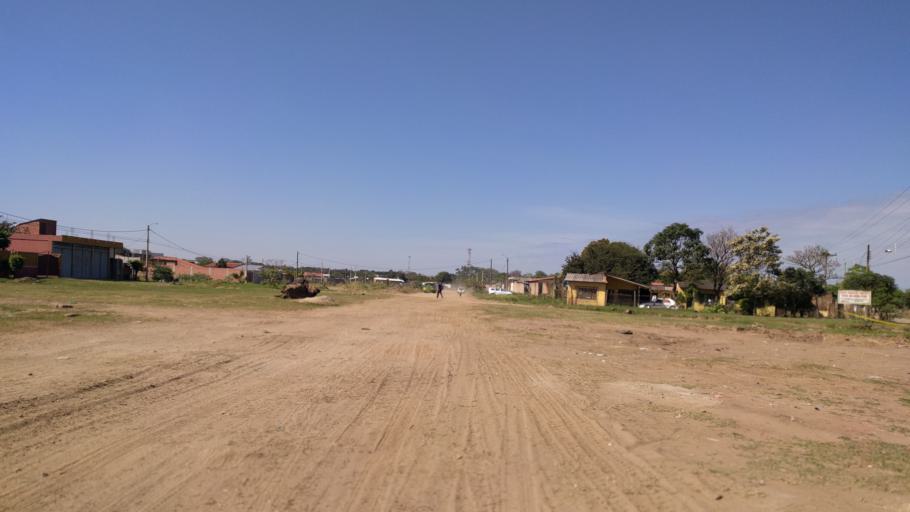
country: BO
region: Santa Cruz
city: Santa Cruz de la Sierra
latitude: -17.8315
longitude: -63.2136
